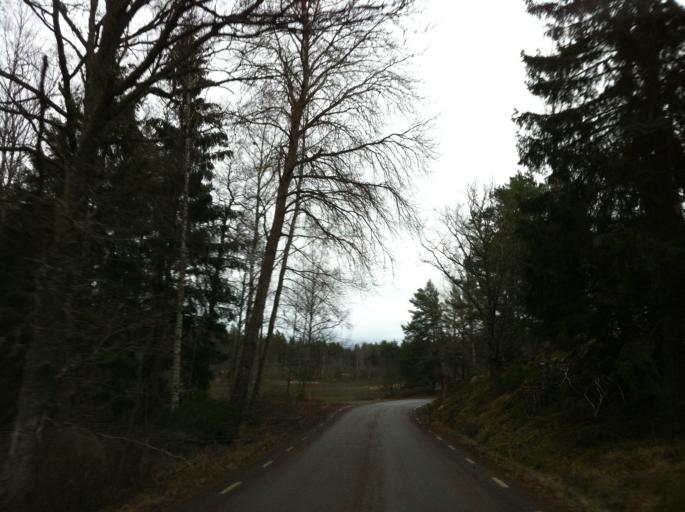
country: SE
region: Kalmar
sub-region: Vasterviks Kommun
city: Forserum
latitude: 57.9264
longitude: 16.5401
